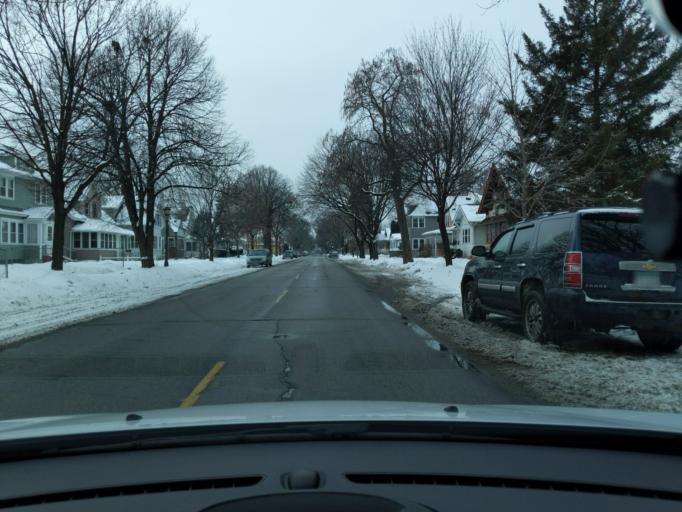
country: US
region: Minnesota
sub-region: Ramsey County
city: Falcon Heights
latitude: 44.9593
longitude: -93.1544
